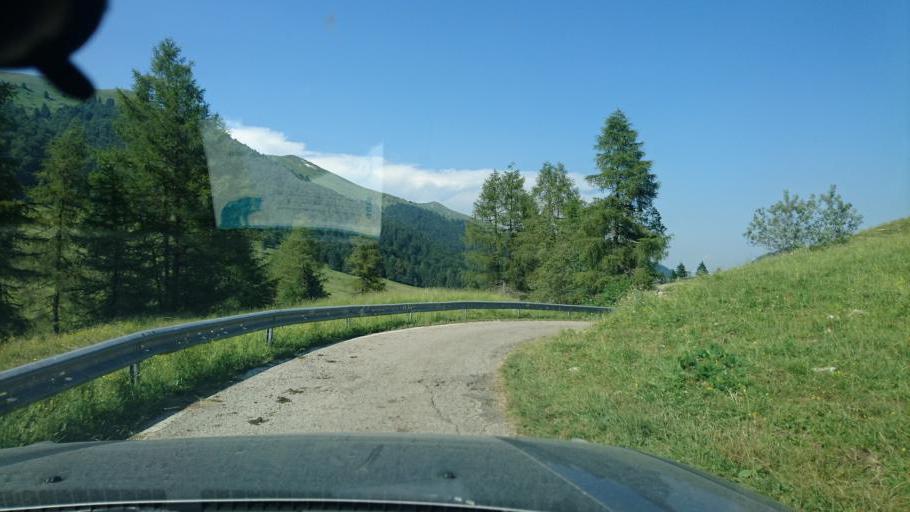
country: IT
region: Veneto
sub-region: Provincia di Treviso
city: Crespano del Grappa
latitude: 45.8916
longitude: 11.8222
